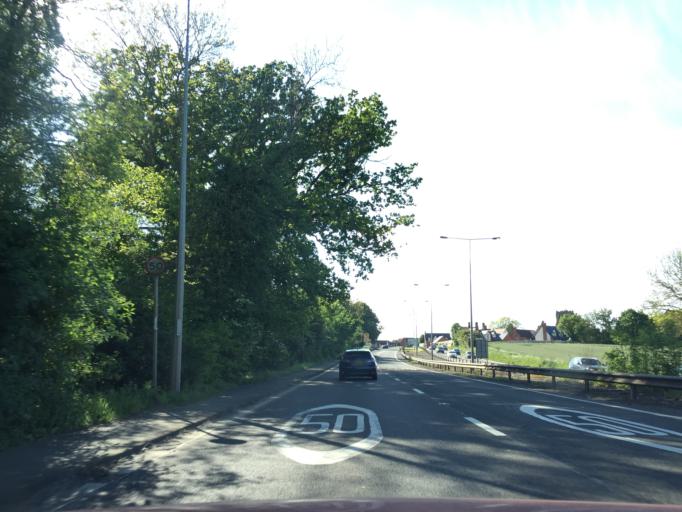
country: GB
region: England
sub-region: Warwickshire
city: Ryton on Dunsmore
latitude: 52.3656
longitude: -1.4307
